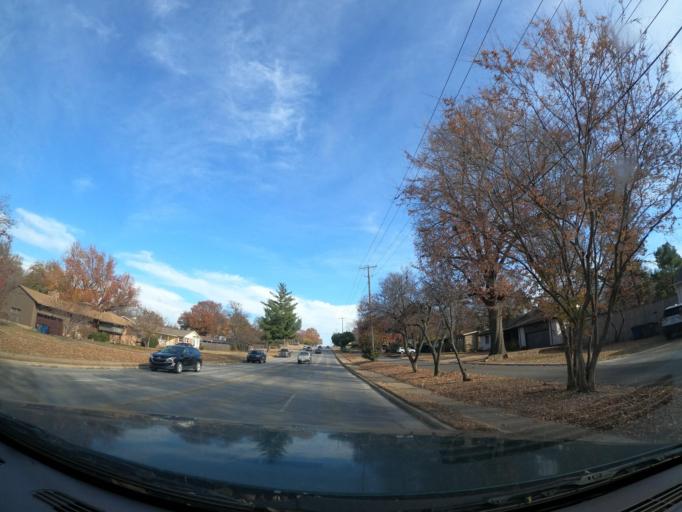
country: US
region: Oklahoma
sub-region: Tulsa County
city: Tulsa
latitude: 36.1043
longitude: -95.9296
